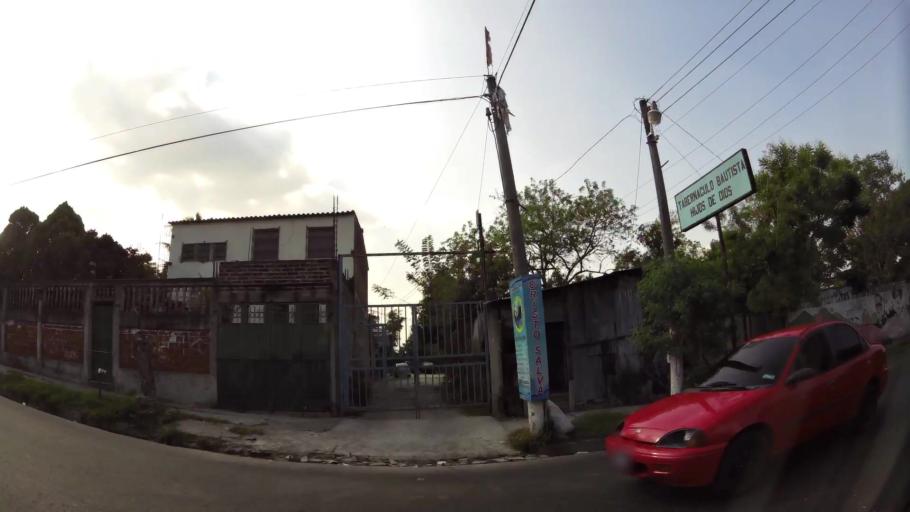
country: SV
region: San Salvador
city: Soyapango
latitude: 13.7265
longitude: -89.1270
